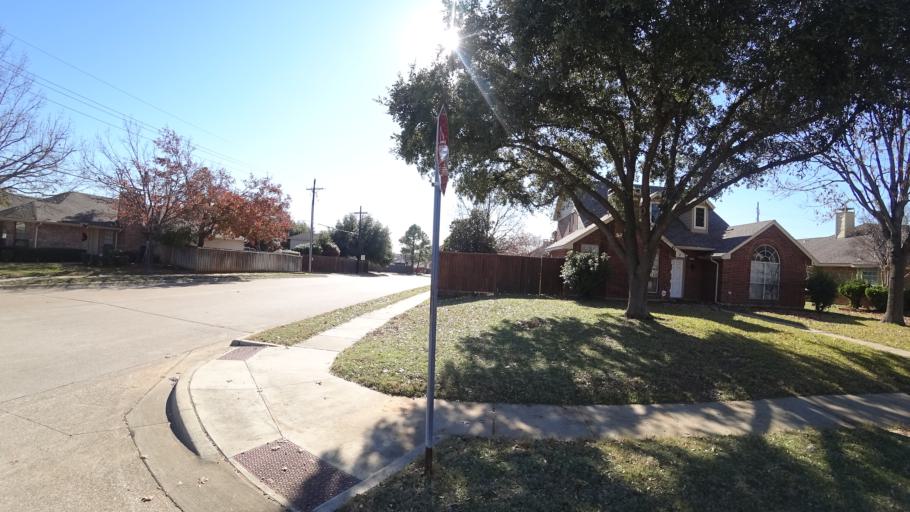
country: US
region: Texas
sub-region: Denton County
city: Lewisville
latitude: 33.0204
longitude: -97.0065
